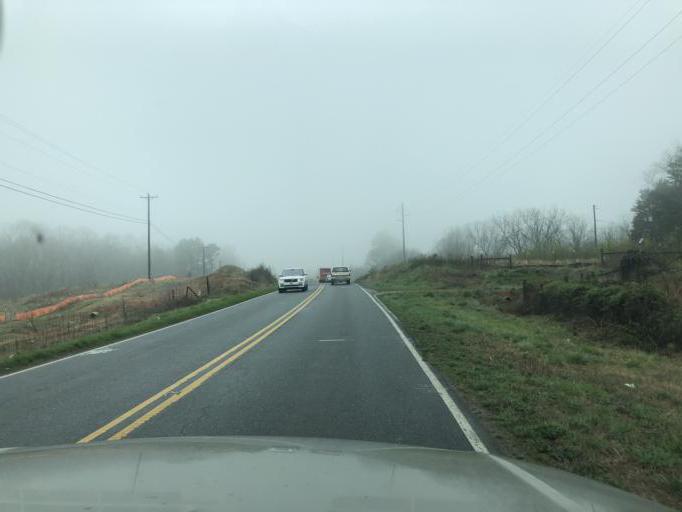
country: US
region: North Carolina
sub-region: Cleveland County
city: Shelby
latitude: 35.3181
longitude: -81.4831
